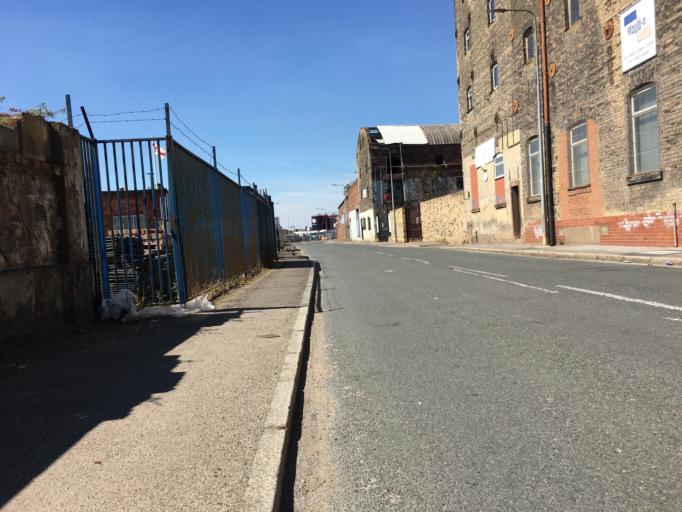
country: GB
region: England
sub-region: City of Kingston upon Hull
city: Hull
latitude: 53.7562
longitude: -0.3321
